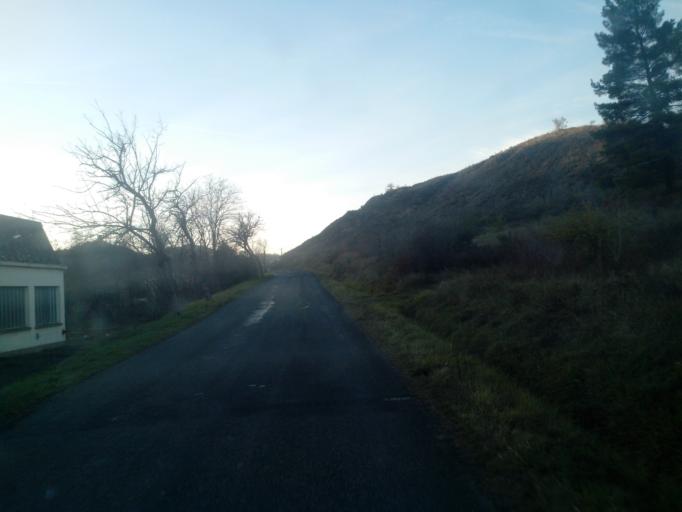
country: FR
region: Languedoc-Roussillon
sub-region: Departement de l'Aude
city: Esperaza
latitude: 42.9339
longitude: 2.2058
